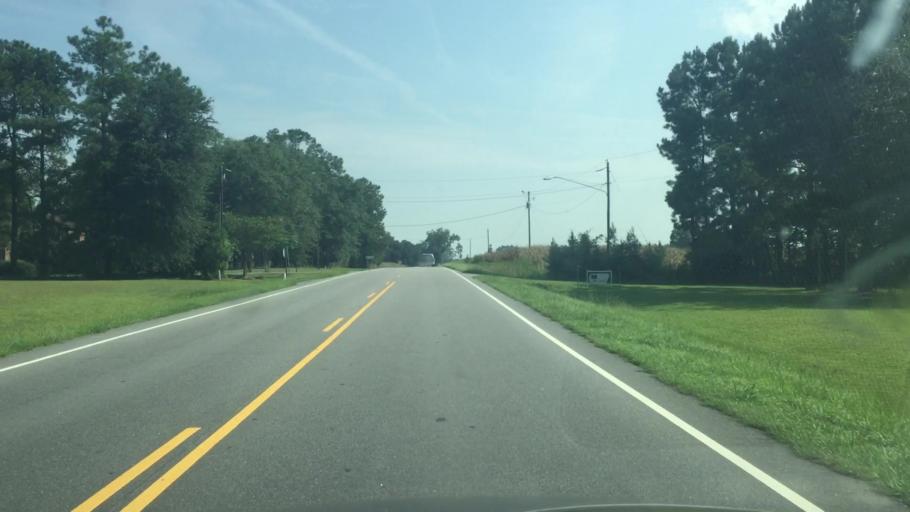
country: US
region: North Carolina
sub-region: Columbus County
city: Tabor City
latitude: 34.1647
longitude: -78.8451
